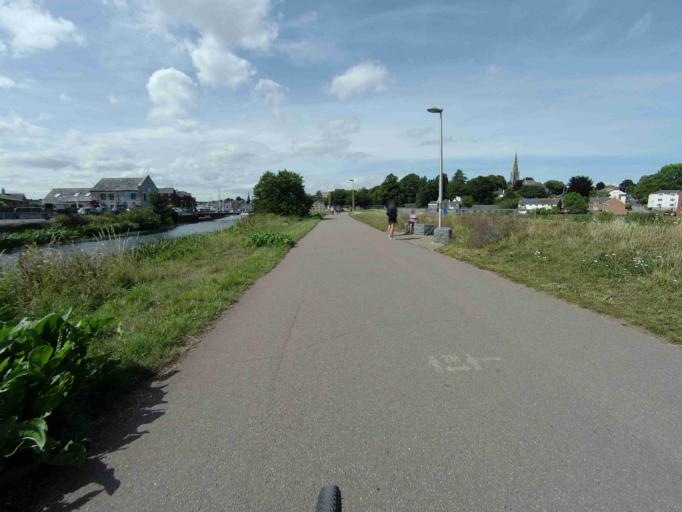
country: GB
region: England
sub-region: Devon
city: Exeter
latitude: 50.7140
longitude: -3.5267
